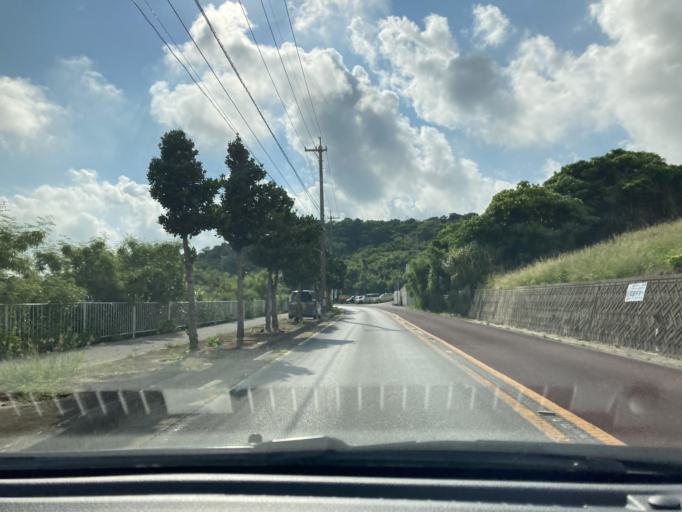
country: JP
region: Okinawa
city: Tomigusuku
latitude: 26.1484
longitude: 127.7563
